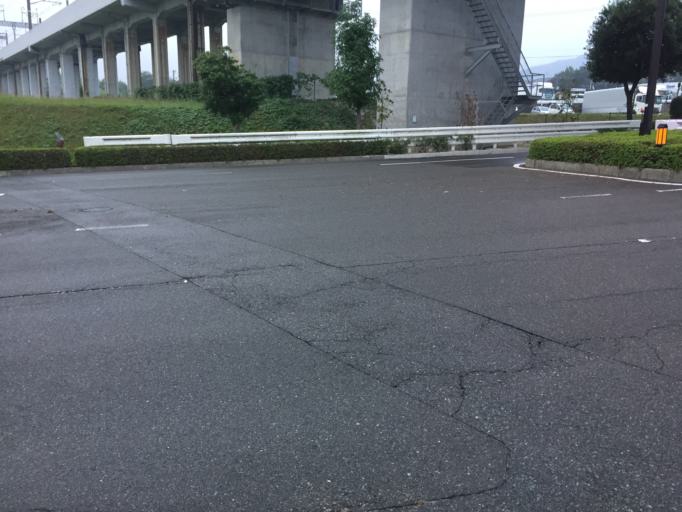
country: JP
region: Hiroshima
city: Takehara
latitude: 34.3918
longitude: 132.7632
